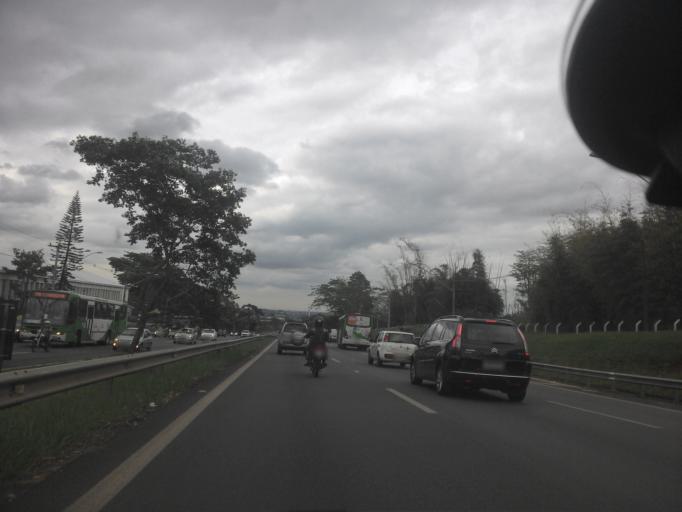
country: BR
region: Sao Paulo
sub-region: Campinas
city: Campinas
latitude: -22.8728
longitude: -47.0687
